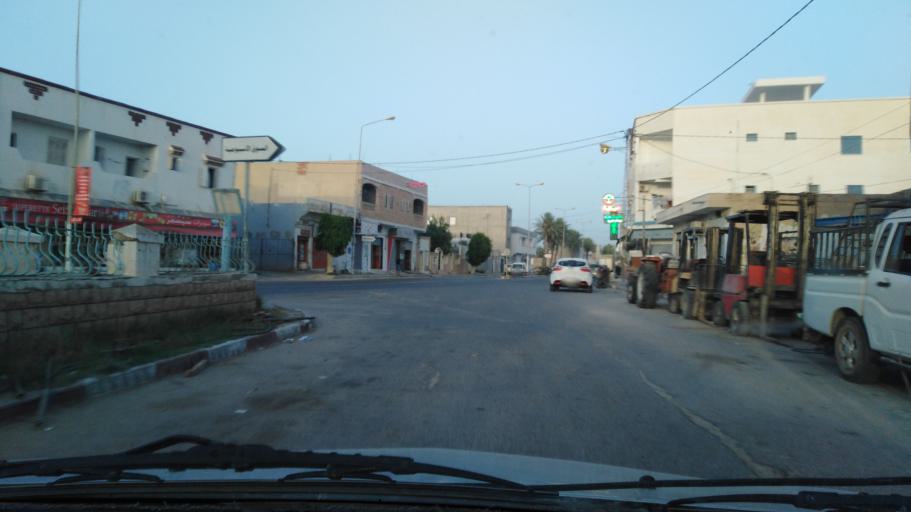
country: TN
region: Qabis
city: Gabes
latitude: 33.9589
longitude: 10.0015
